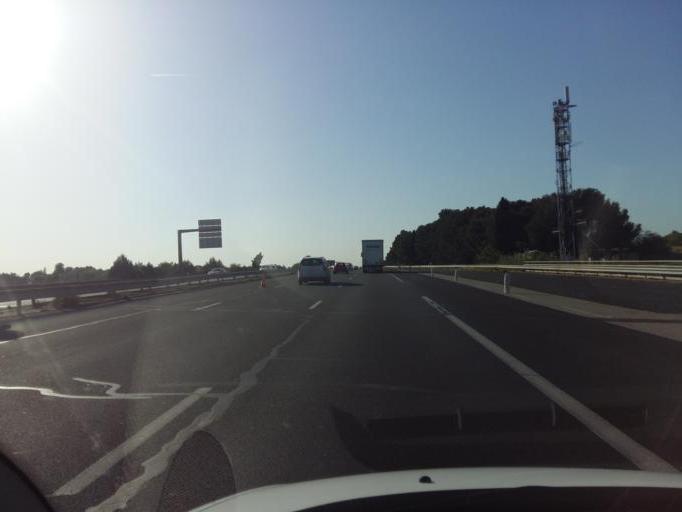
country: FR
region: Provence-Alpes-Cote d'Azur
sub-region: Departement des Bouches-du-Rhone
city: Aix-en-Provence
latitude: 43.5267
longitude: 5.4026
